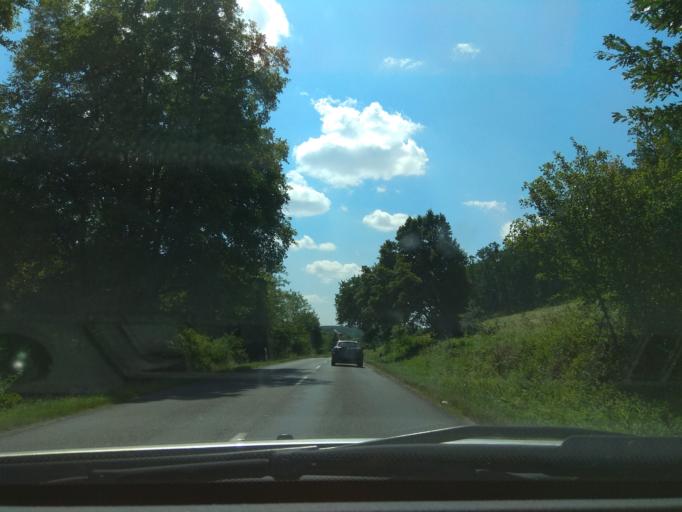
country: HU
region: Borsod-Abauj-Zemplen
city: Harsany
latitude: 48.0077
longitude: 20.7623
